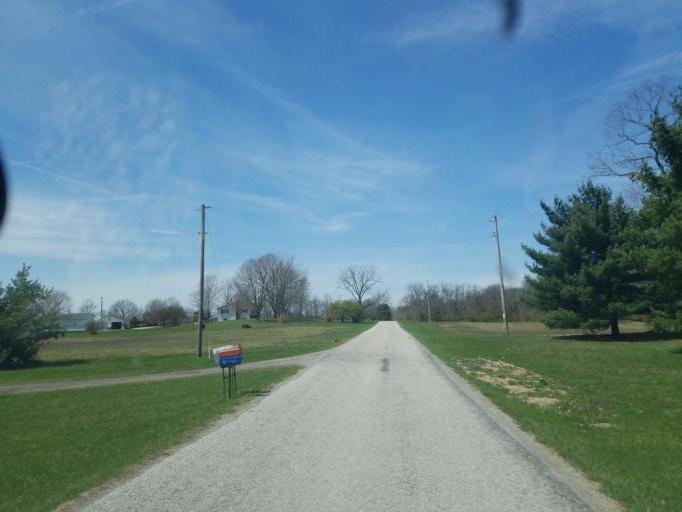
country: US
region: Ohio
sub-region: Delaware County
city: Ashley
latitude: 40.4294
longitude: -83.0653
